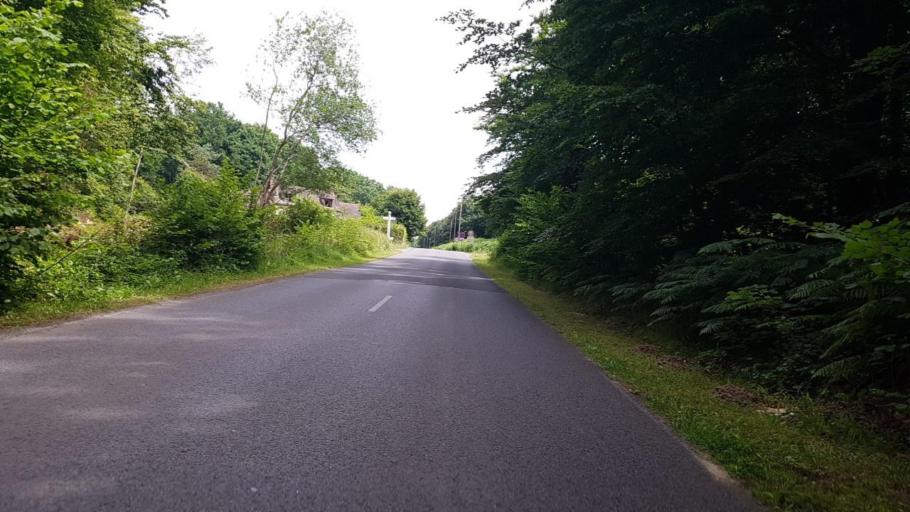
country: FR
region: Picardie
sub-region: Departement de l'Oise
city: Montmacq
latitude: 49.4771
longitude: 2.9286
